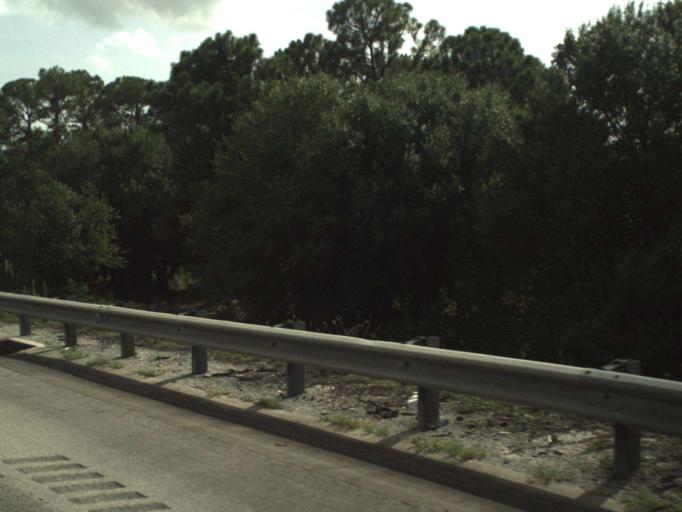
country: US
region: Florida
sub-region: Saint Lucie County
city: Fort Pierce South
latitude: 27.3723
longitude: -80.4113
